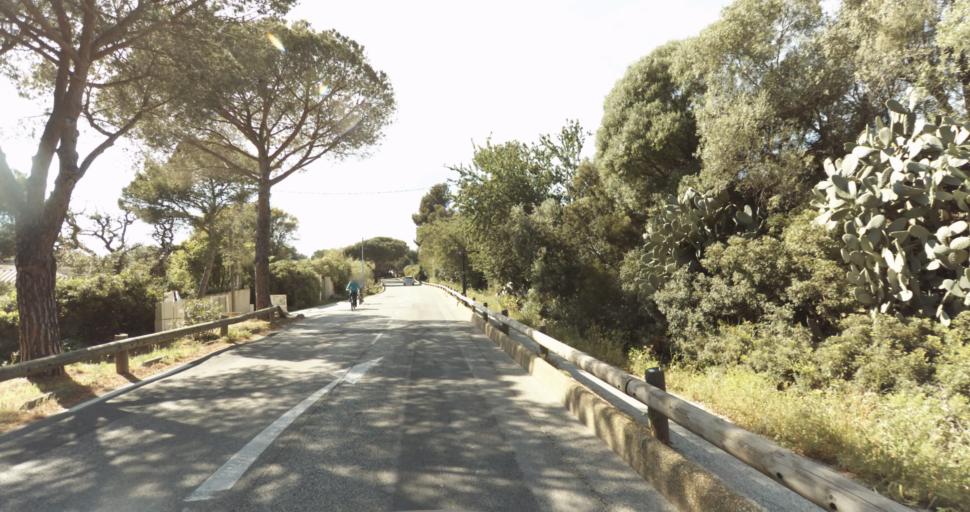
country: FR
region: Provence-Alpes-Cote d'Azur
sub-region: Departement du Var
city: Hyeres
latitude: 43.0312
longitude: 6.1526
